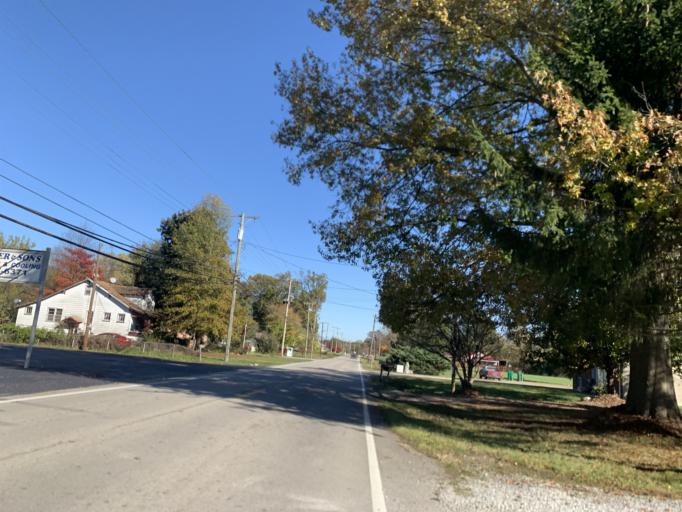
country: US
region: Kentucky
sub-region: Jefferson County
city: Pleasure Ridge Park
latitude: 38.1475
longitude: -85.8942
